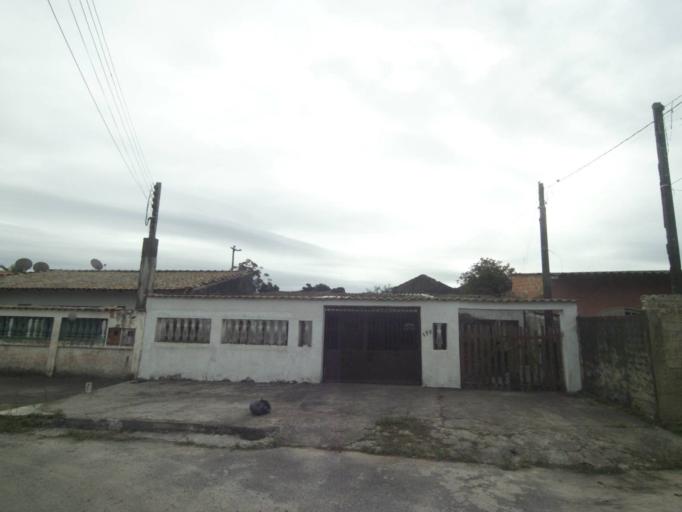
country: BR
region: Parana
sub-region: Paranagua
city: Paranagua
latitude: -25.5172
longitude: -48.5283
